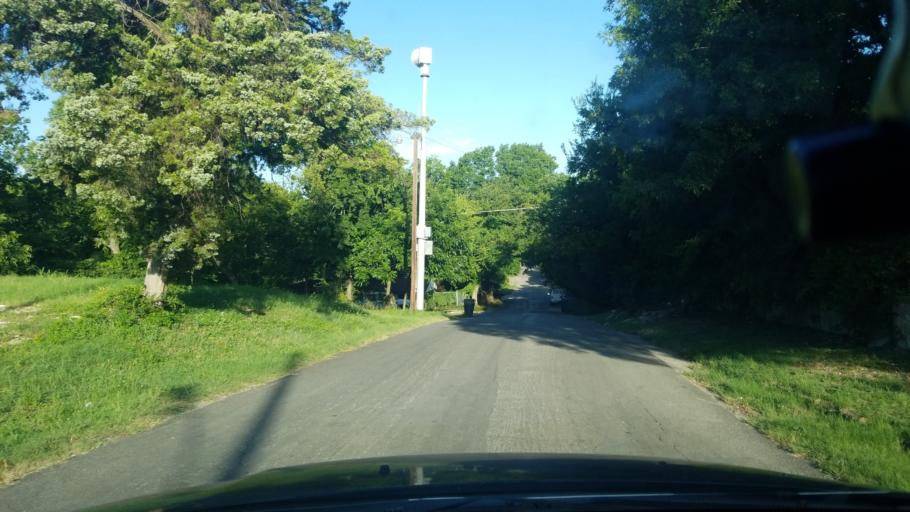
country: US
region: Texas
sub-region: Dallas County
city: Dallas
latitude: 32.7264
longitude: -96.8182
